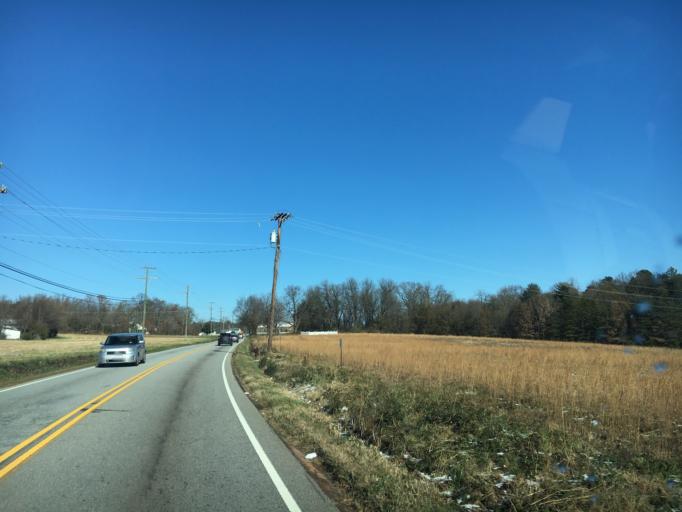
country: US
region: South Carolina
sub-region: Greenville County
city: Taylors
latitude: 34.9210
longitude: -82.2689
